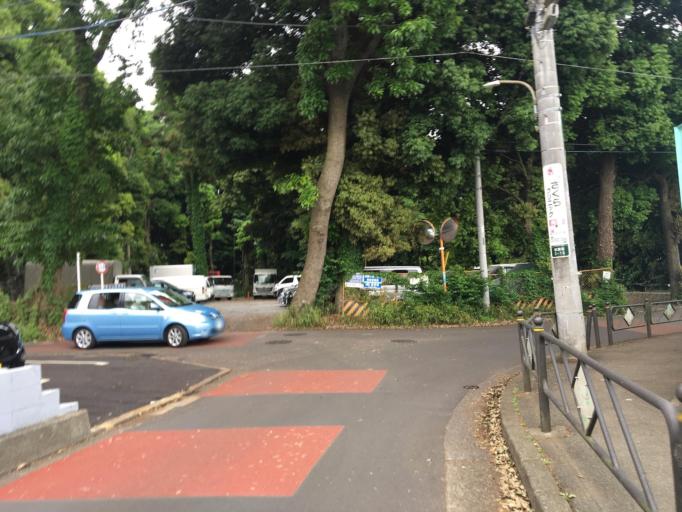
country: JP
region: Tokyo
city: Chofugaoka
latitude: 35.6538
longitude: 139.5842
